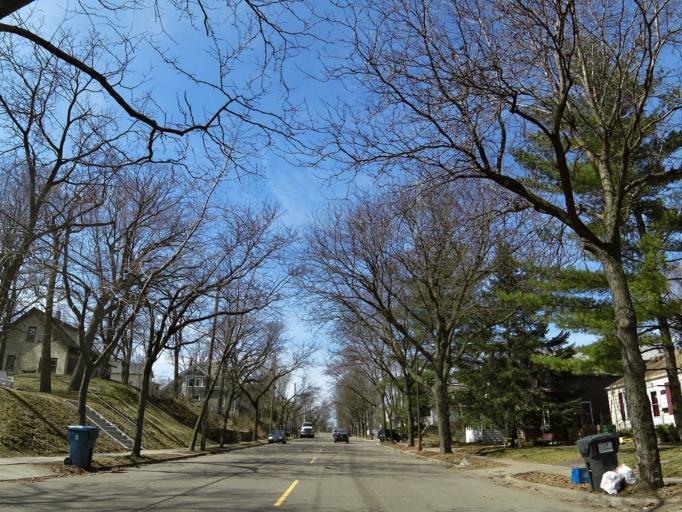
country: US
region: Minnesota
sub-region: Ramsey County
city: Saint Paul
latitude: 44.9488
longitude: -93.0523
